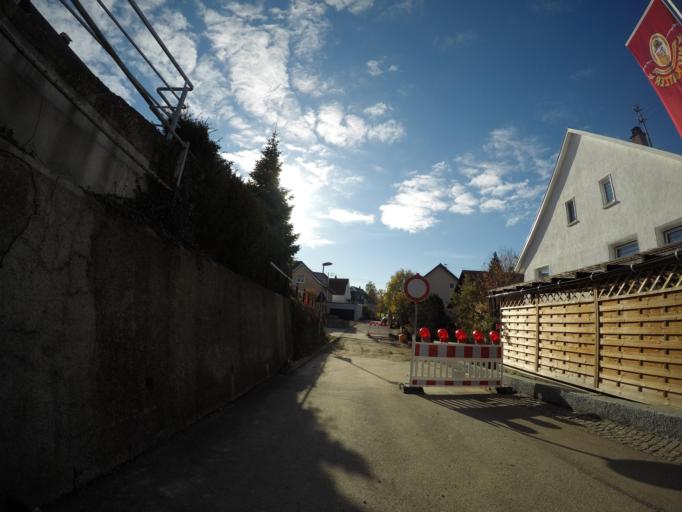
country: DE
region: Baden-Wuerttemberg
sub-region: Tuebingen Region
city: Herbertingen
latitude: 48.0565
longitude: 9.4423
